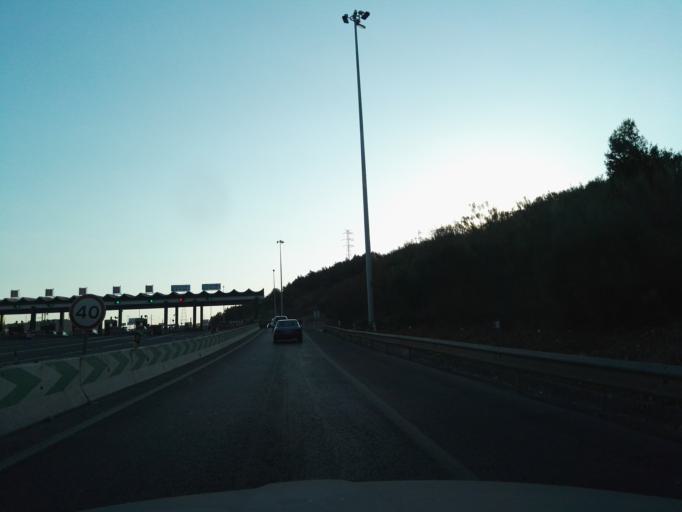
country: PT
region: Lisbon
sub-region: Vila Franca de Xira
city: Vialonga
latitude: 38.8887
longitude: -9.0544
